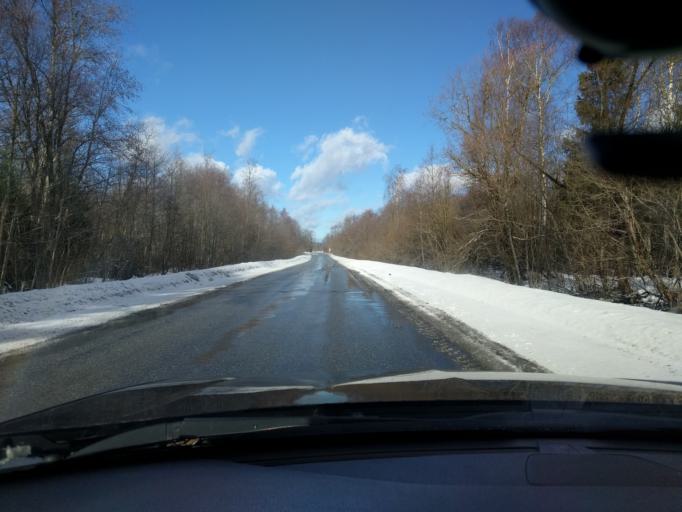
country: EE
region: Harju
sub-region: Raasiku vald
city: Raasiku
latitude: 59.3056
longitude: 25.1696
